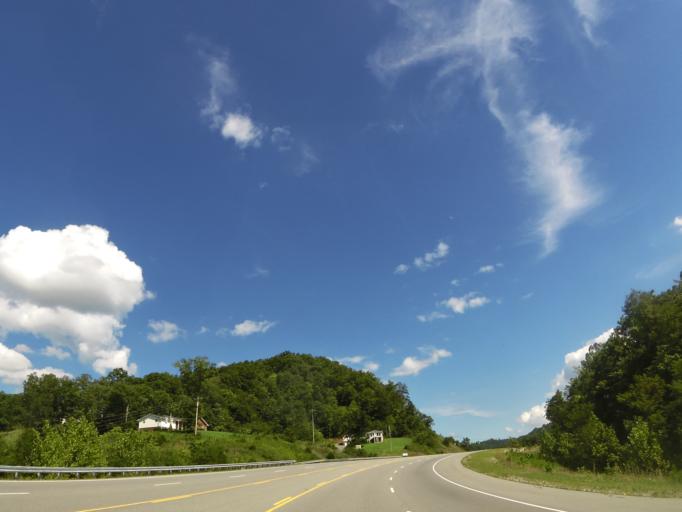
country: US
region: Tennessee
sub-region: Claiborne County
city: Tazewell
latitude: 36.4190
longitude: -83.5143
